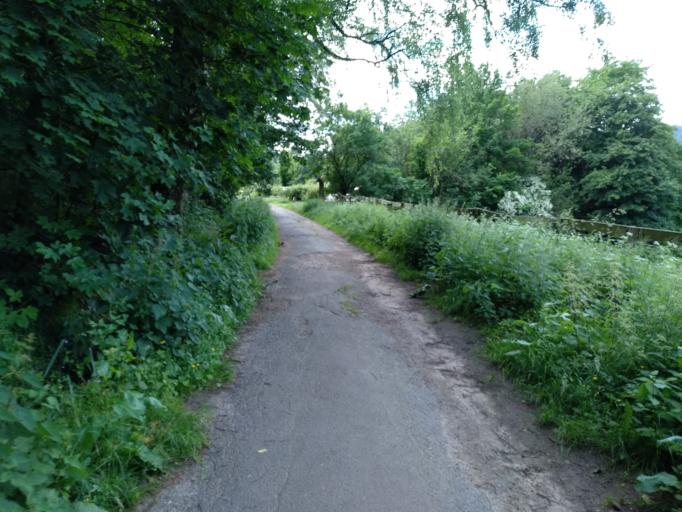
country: DE
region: Hesse
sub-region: Regierungsbezirk Giessen
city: Marburg an der Lahn
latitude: 50.8206
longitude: 8.7871
